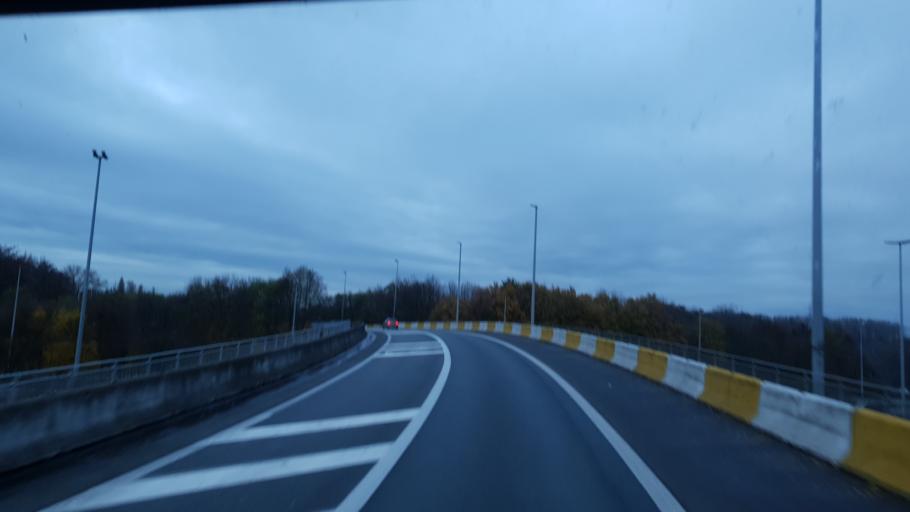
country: BE
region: Flanders
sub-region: Provincie Oost-Vlaanderen
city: Destelbergen
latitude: 51.0499
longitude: 3.8233
